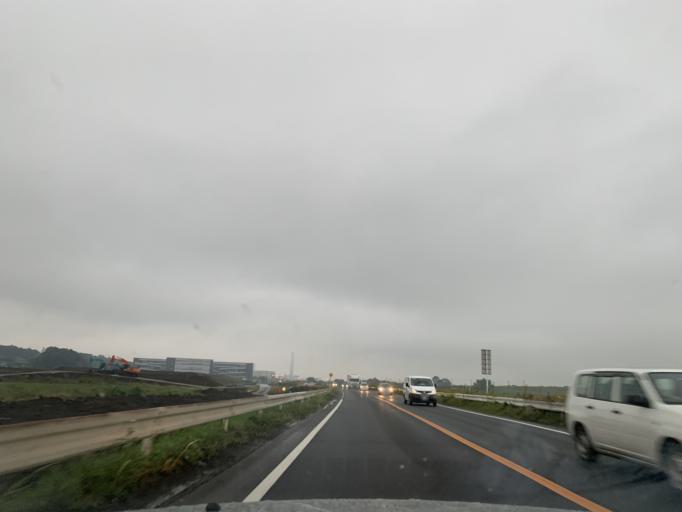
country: JP
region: Chiba
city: Nagareyama
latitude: 35.8951
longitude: 139.8930
